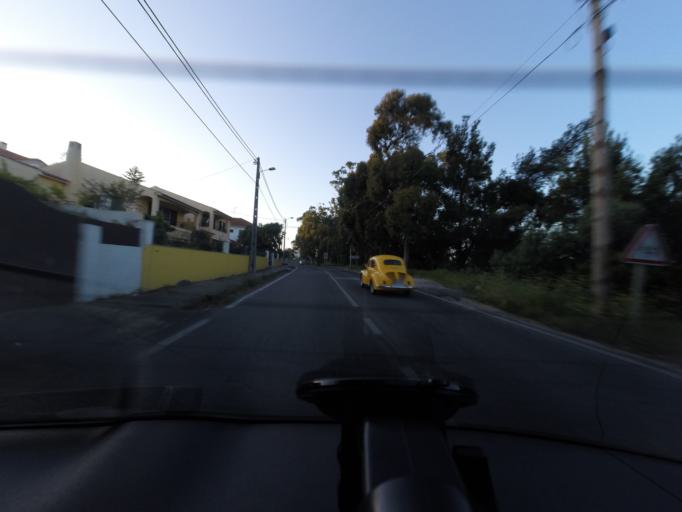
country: PT
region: Lisbon
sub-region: Sintra
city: Rio de Mouro
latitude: 38.7567
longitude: -9.3449
